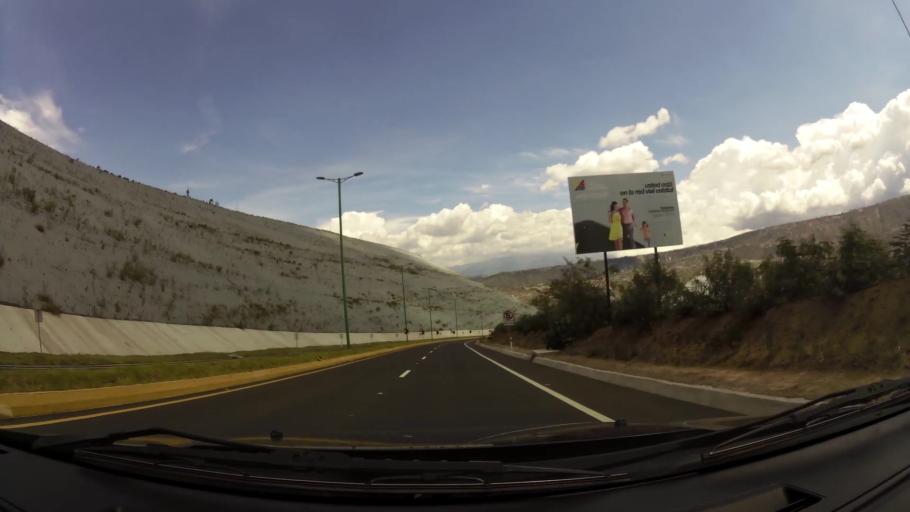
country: EC
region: Pichincha
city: Quito
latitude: -0.0995
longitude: -78.3673
